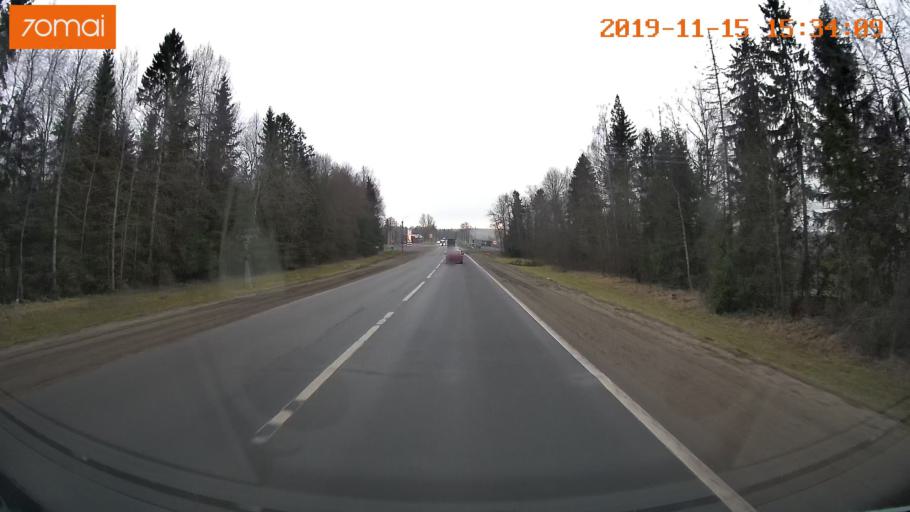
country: RU
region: Jaroslavl
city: Danilov
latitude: 58.0724
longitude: 40.0899
